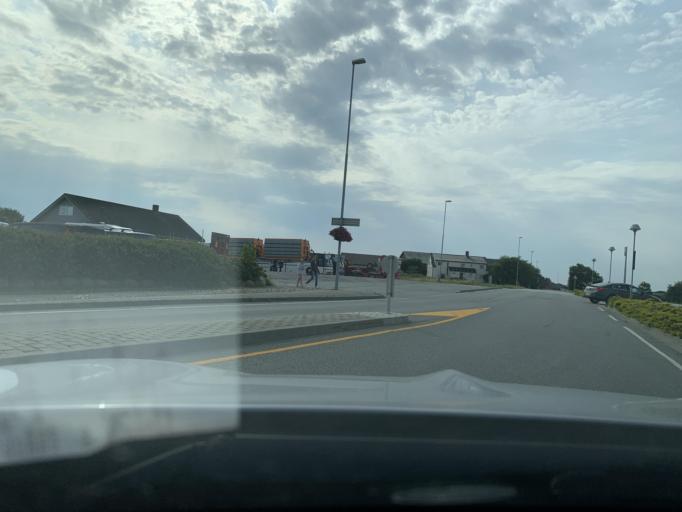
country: NO
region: Rogaland
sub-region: Time
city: Bryne
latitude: 58.7181
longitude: 5.5685
